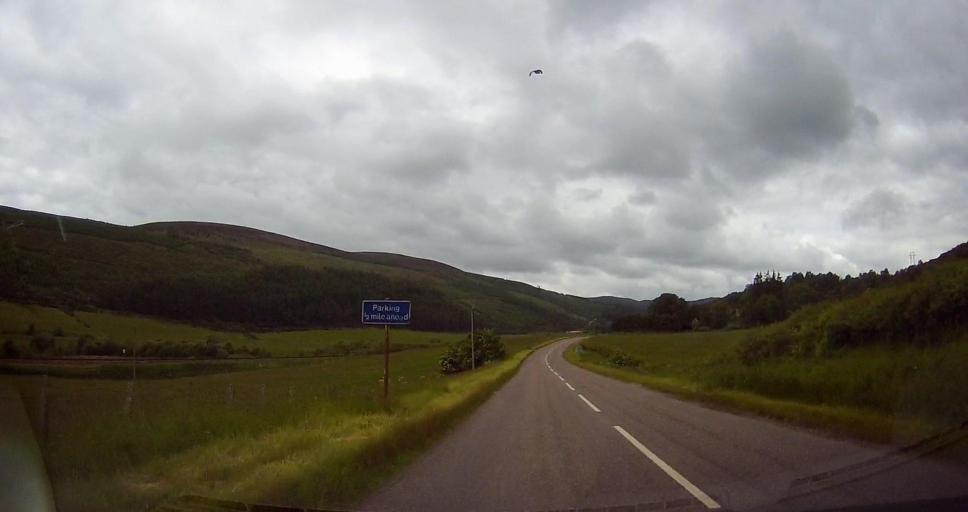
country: GB
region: Scotland
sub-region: Highland
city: Dornoch
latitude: 57.9836
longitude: -4.1410
